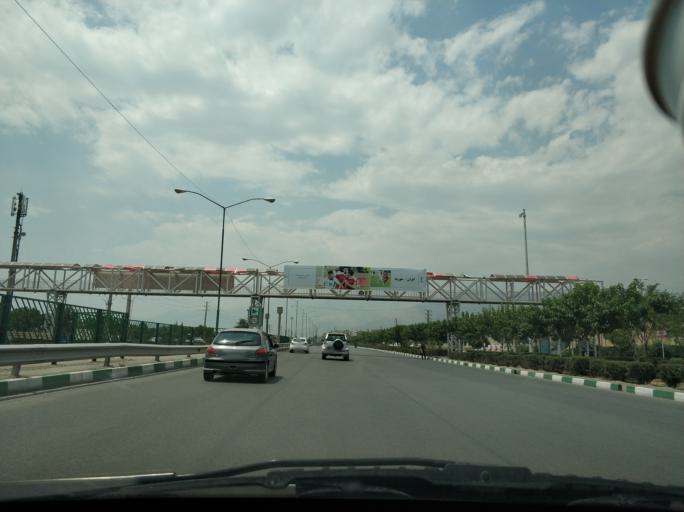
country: IR
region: Tehran
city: Tajrish
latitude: 35.7611
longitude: 51.5709
